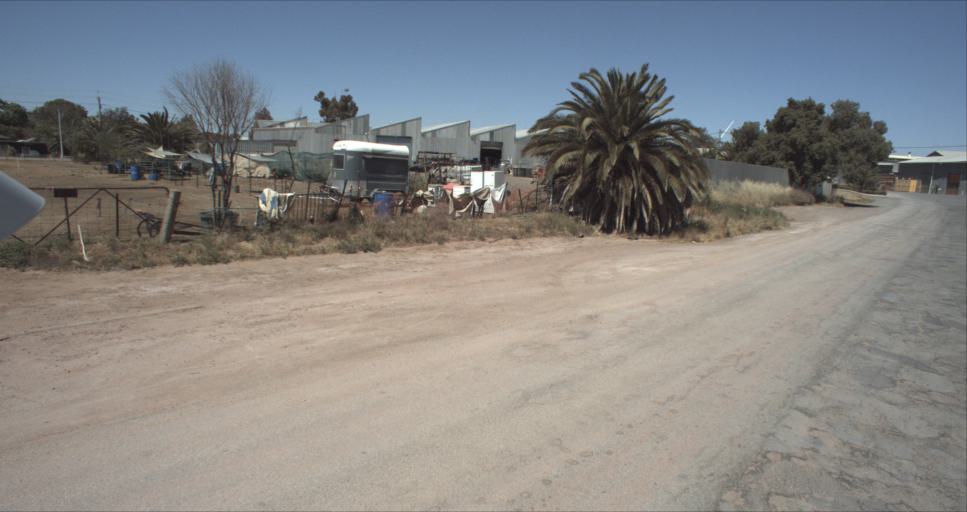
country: AU
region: New South Wales
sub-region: Leeton
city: Leeton
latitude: -34.5488
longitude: 146.3971
